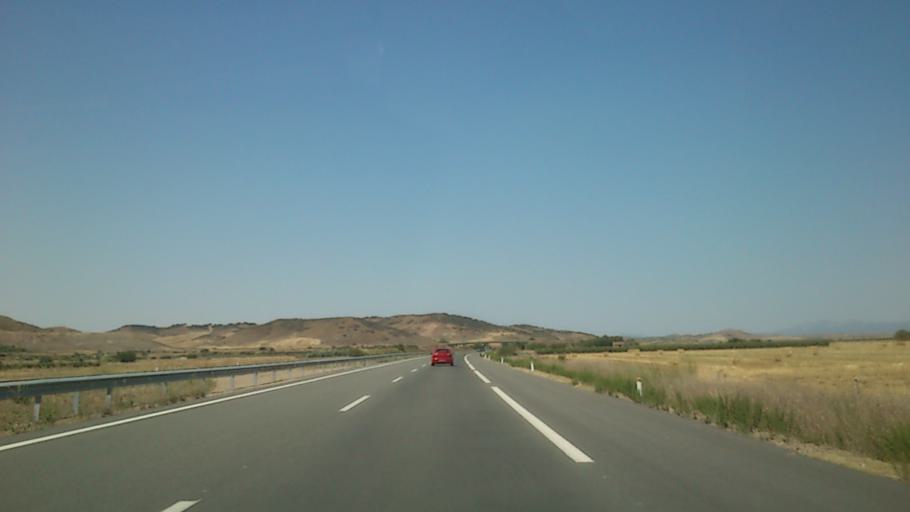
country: ES
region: La Rioja
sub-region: Provincia de La Rioja
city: Pradejon
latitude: 42.3436
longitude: -2.0394
